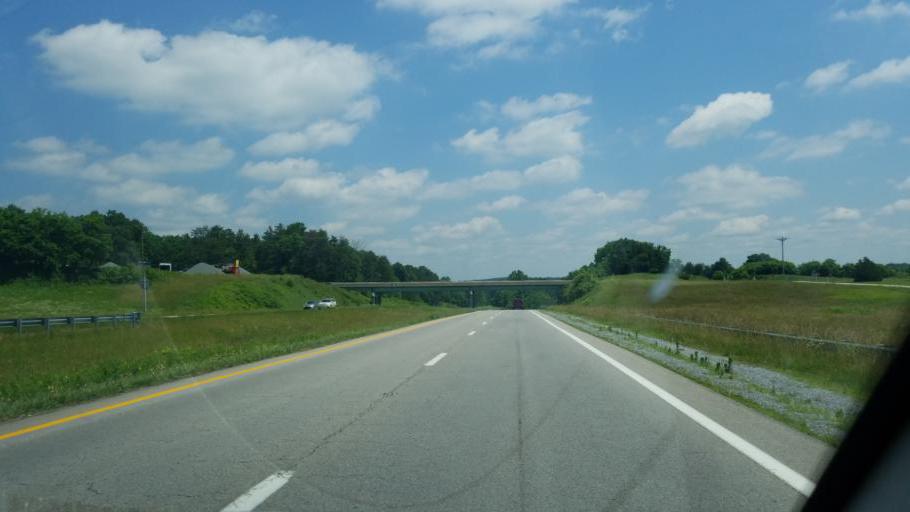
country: US
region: Virginia
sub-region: Pittsylvania County
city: Hurt
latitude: 37.1128
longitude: -79.3279
